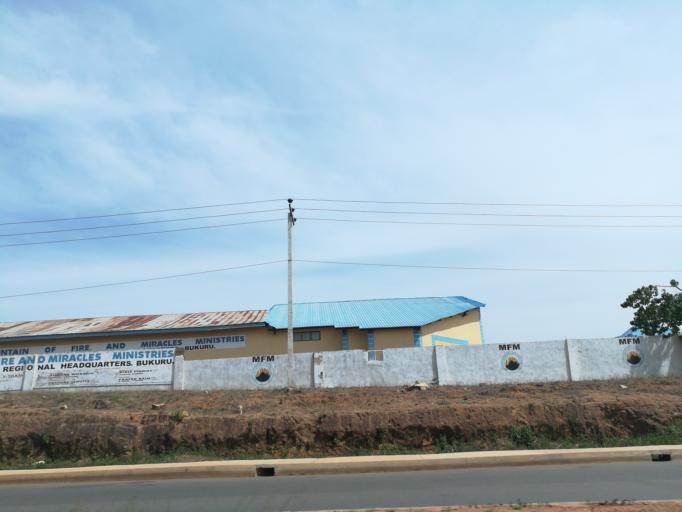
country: NG
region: Plateau
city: Bukuru
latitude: 9.8230
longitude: 8.8651
